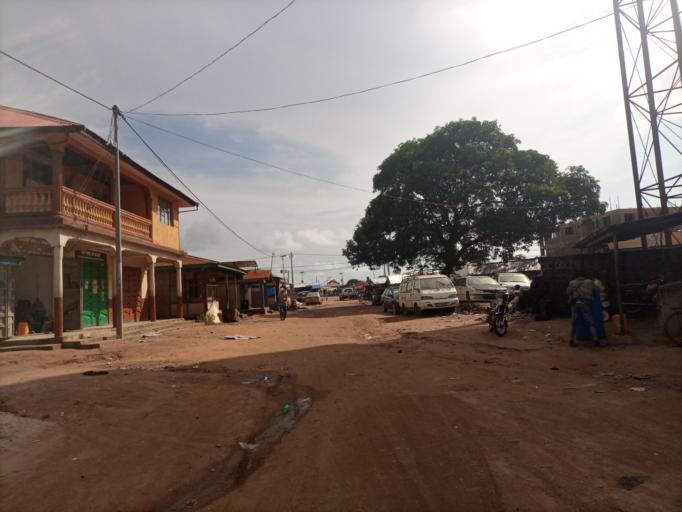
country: SL
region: Northern Province
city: Masoyila
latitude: 8.6043
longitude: -13.1790
